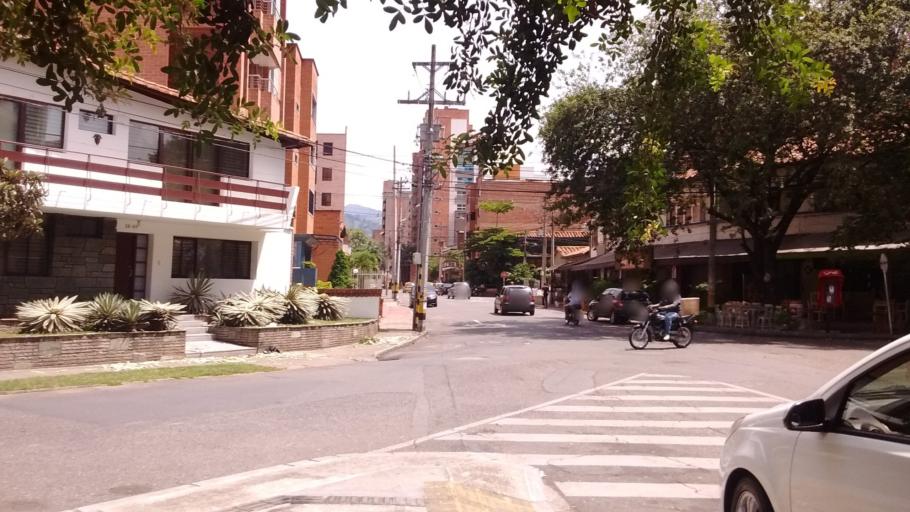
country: CO
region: Antioquia
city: Medellin
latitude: 6.2455
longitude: -75.5970
